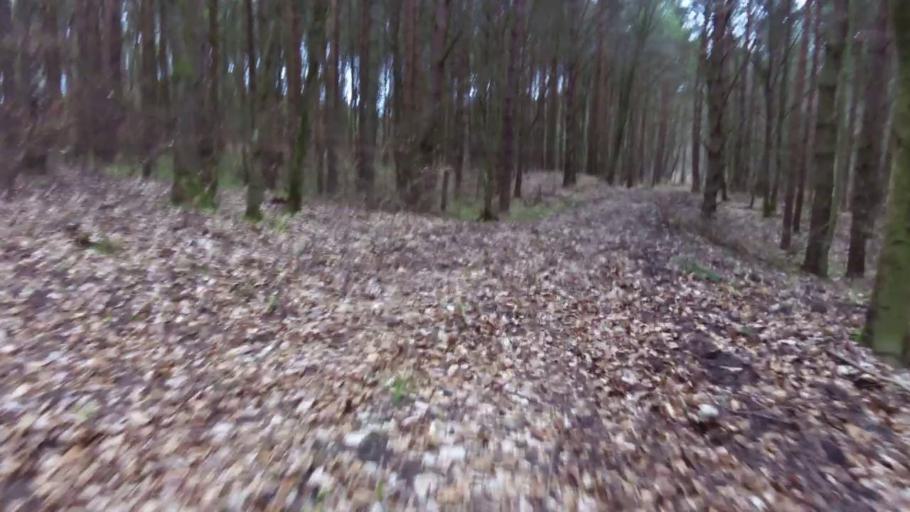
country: PL
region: West Pomeranian Voivodeship
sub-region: Powiat kamienski
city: Wolin
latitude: 53.9849
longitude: 14.6063
